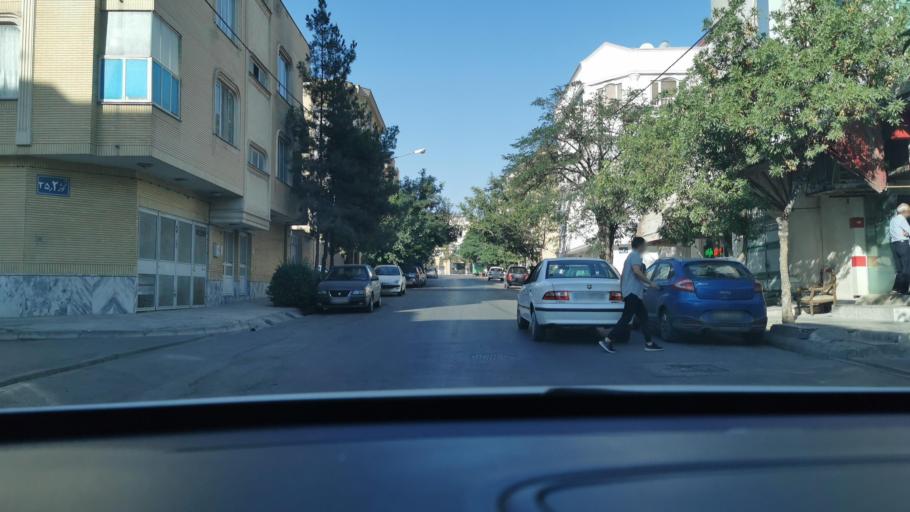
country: IR
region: Razavi Khorasan
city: Mashhad
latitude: 36.3099
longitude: 59.5107
